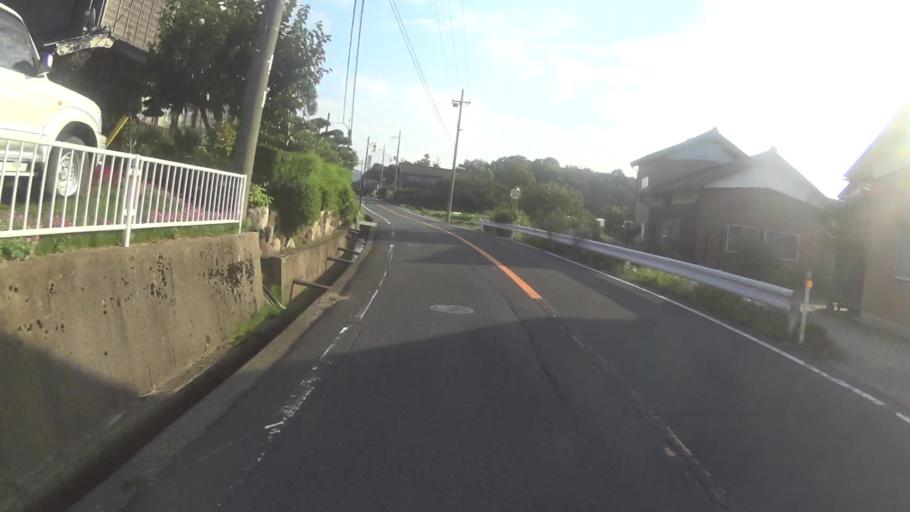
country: JP
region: Kyoto
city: Miyazu
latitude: 35.6654
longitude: 135.0912
